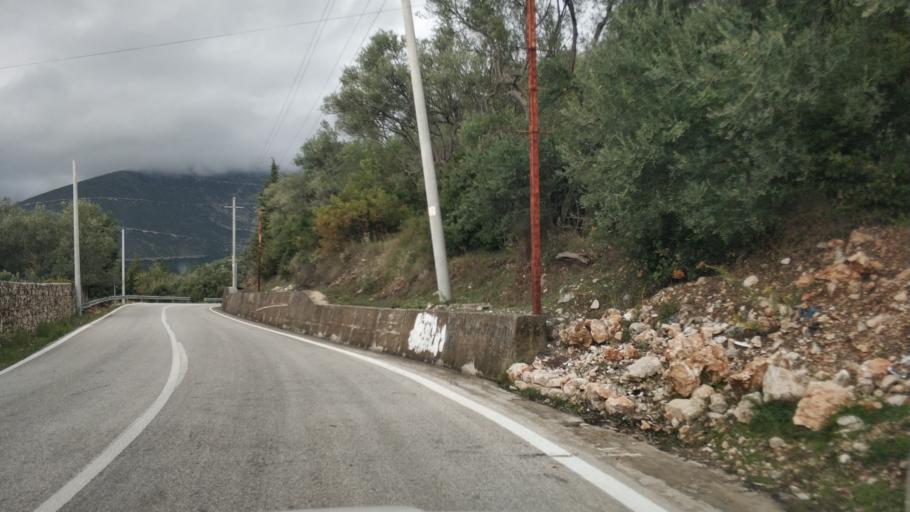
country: AL
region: Vlore
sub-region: Rrethi i Vlores
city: Vranisht
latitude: 40.1643
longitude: 19.6209
